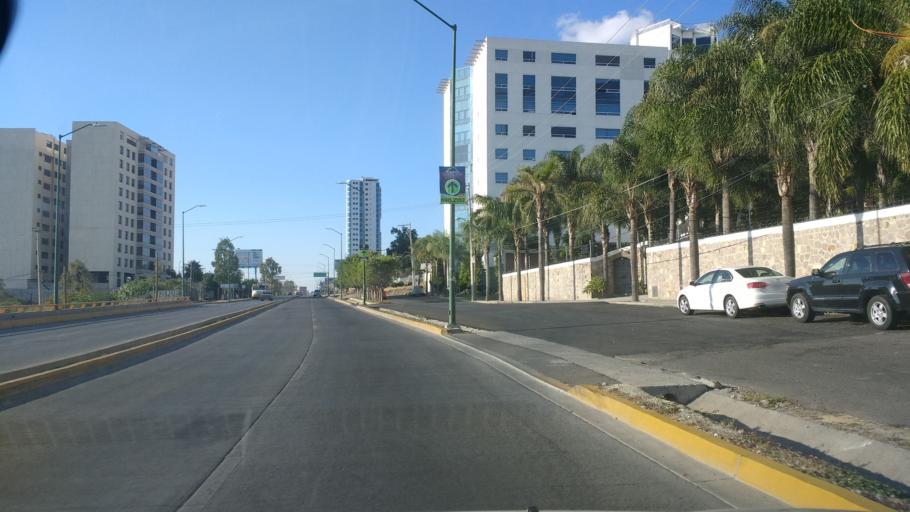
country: MX
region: Guanajuato
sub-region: Leon
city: La Ermita
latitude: 21.1556
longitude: -101.7203
